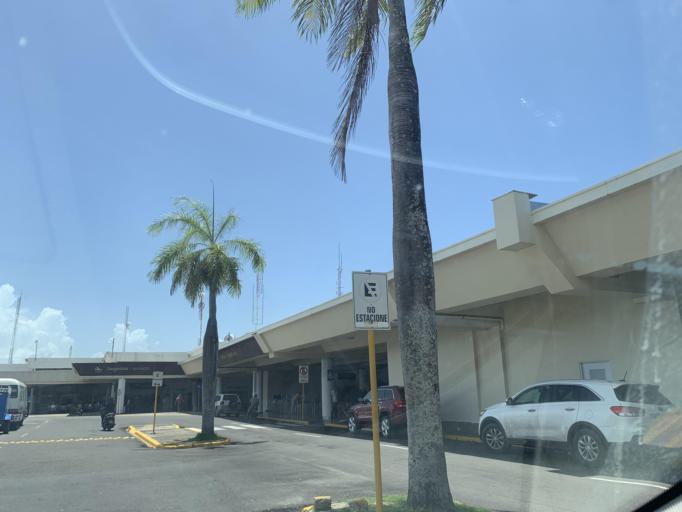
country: DO
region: Puerto Plata
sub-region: Puerto Plata
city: Puerto Plata
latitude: 19.7553
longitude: -70.5627
